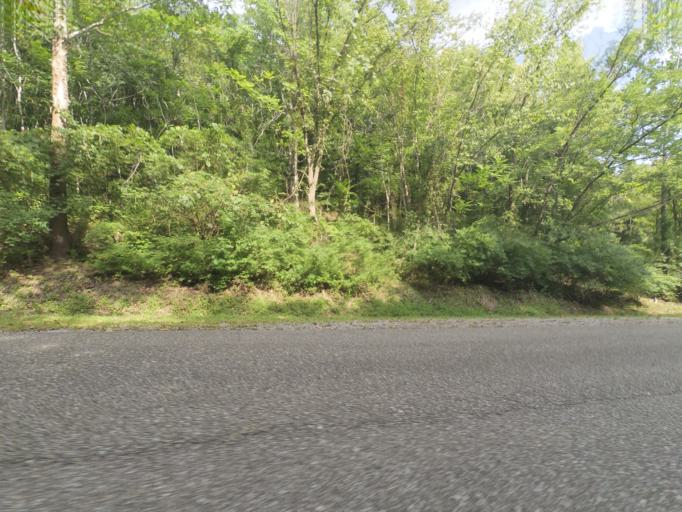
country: US
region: West Virginia
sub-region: Cabell County
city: Huntington
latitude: 38.4166
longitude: -82.3938
